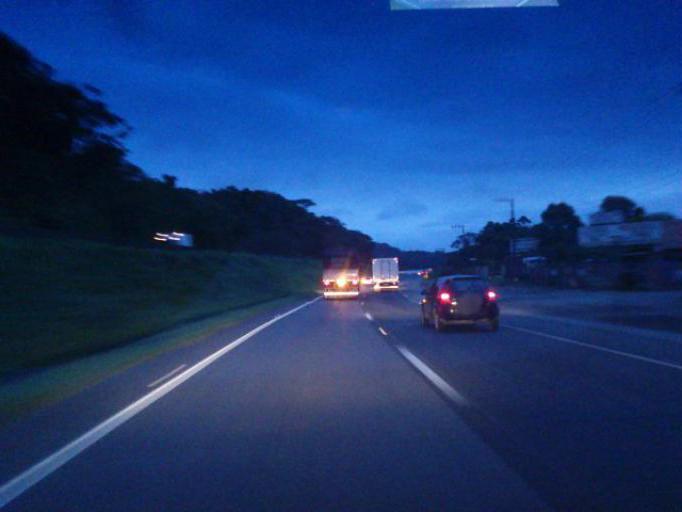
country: BR
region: Santa Catarina
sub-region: Navegantes
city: Navegantes
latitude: -26.8335
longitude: -48.6966
